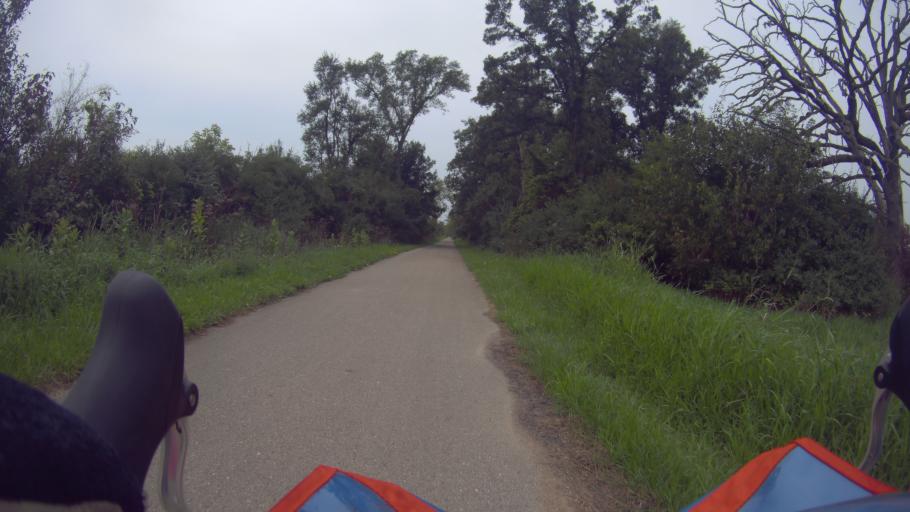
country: US
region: Wisconsin
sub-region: Dane County
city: Verona
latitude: 42.9978
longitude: -89.4977
